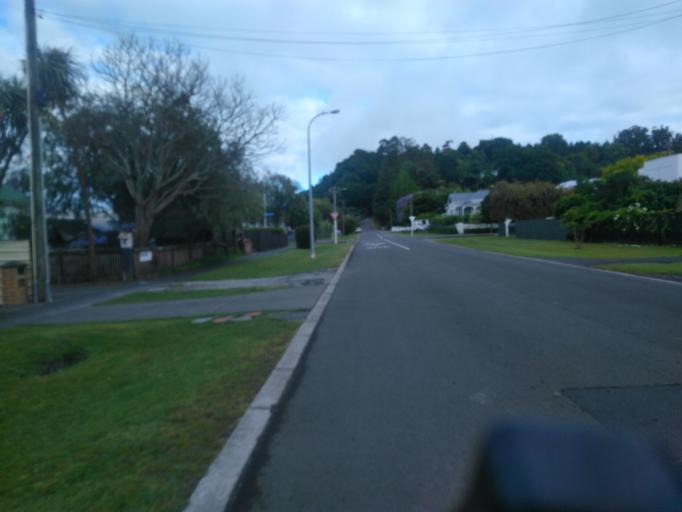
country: NZ
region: Gisborne
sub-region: Gisborne District
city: Gisborne
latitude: -38.6540
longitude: 178.0277
